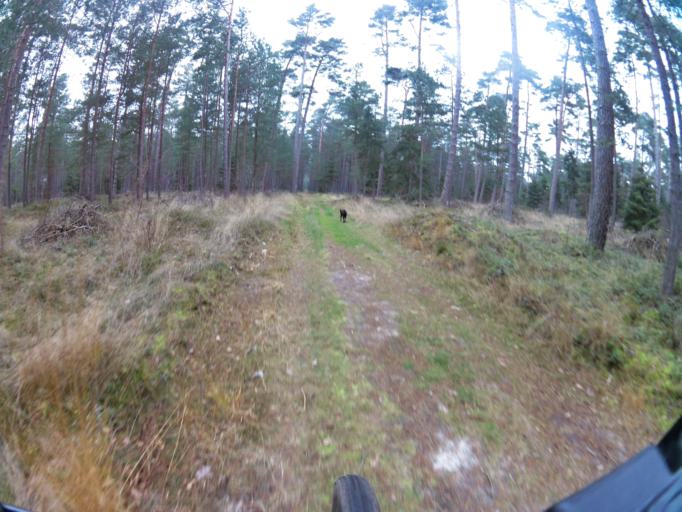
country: PL
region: West Pomeranian Voivodeship
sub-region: Powiat gryficki
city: Cerkwica
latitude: 54.1063
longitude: 15.1436
